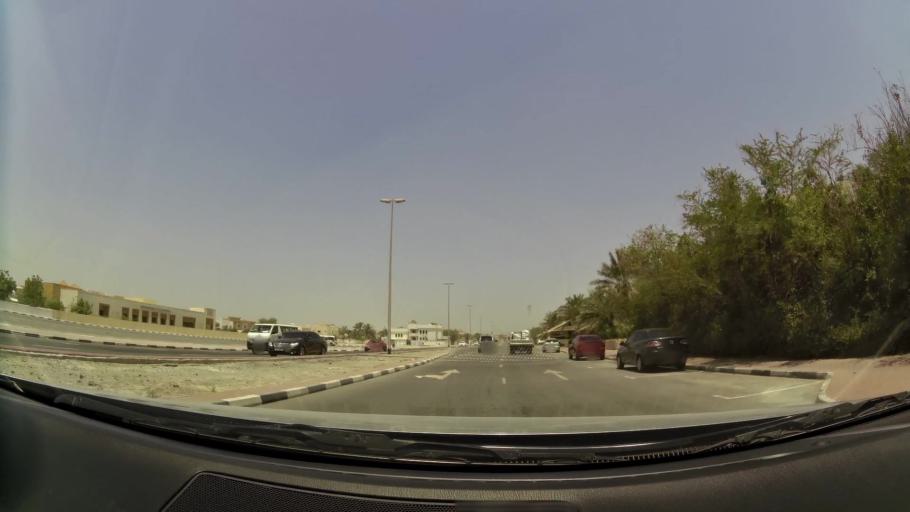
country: AE
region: Dubai
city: Dubai
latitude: 25.1945
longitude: 55.2544
